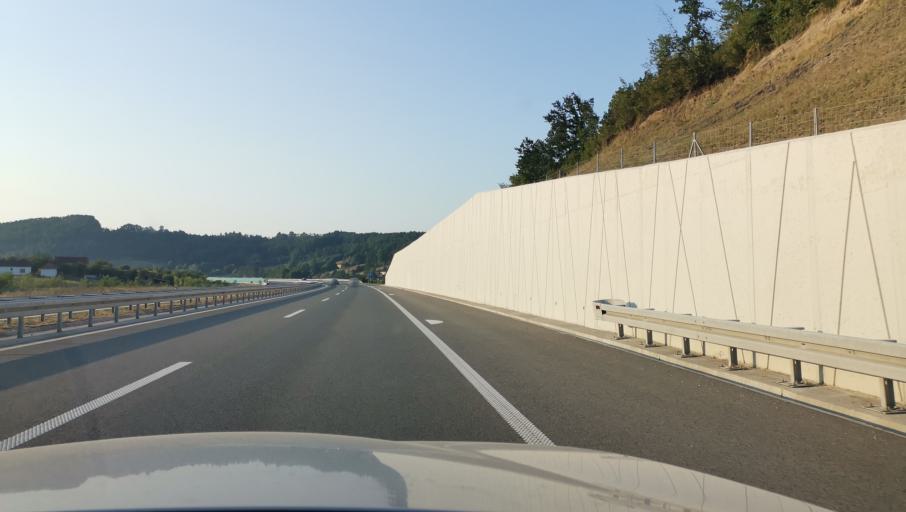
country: RS
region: Central Serbia
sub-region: Kolubarski Okrug
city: Ljig
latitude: 44.1621
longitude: 20.3169
